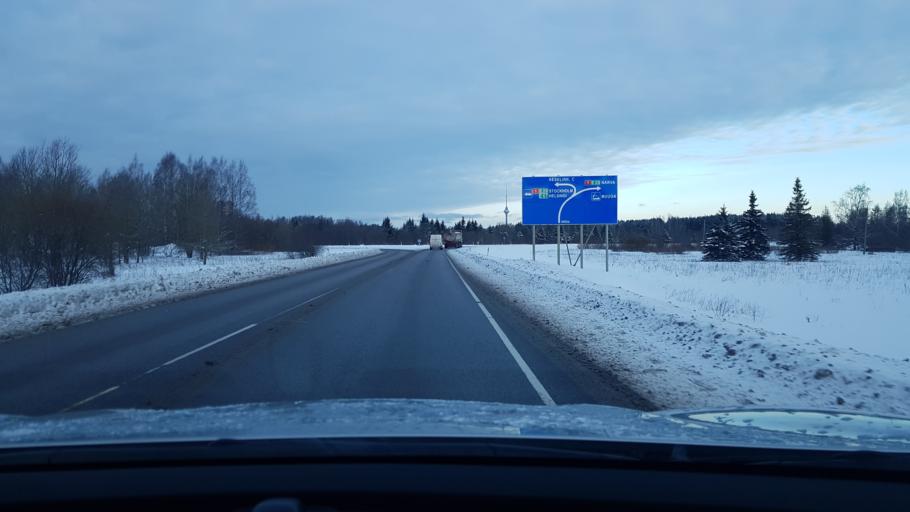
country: EE
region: Harju
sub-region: Joelaehtme vald
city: Loo
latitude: 59.4396
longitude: 24.9115
